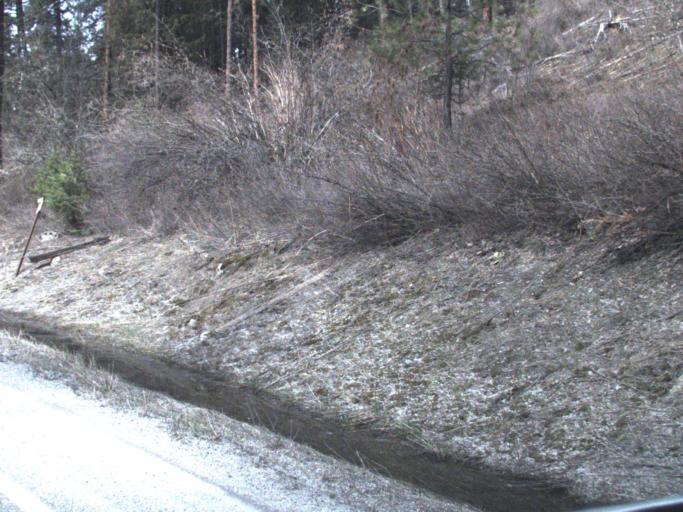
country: US
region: Washington
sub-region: Pend Oreille County
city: Newport
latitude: 48.4702
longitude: -117.3144
